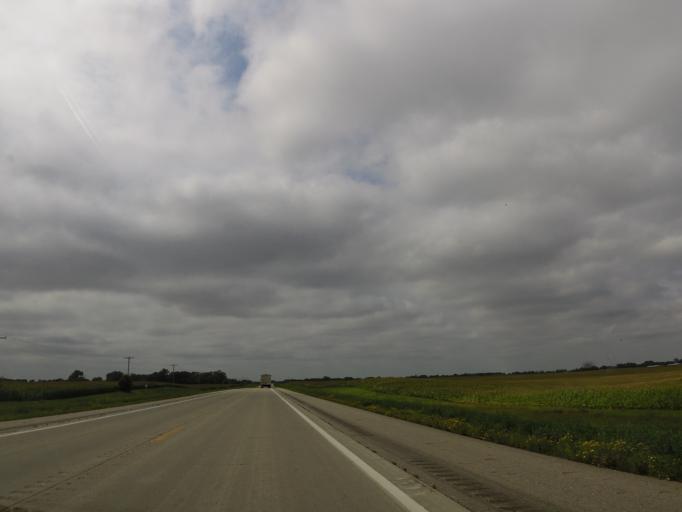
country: US
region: Minnesota
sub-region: Lac qui Parle County
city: Dawson
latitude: 44.9362
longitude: -96.0078
